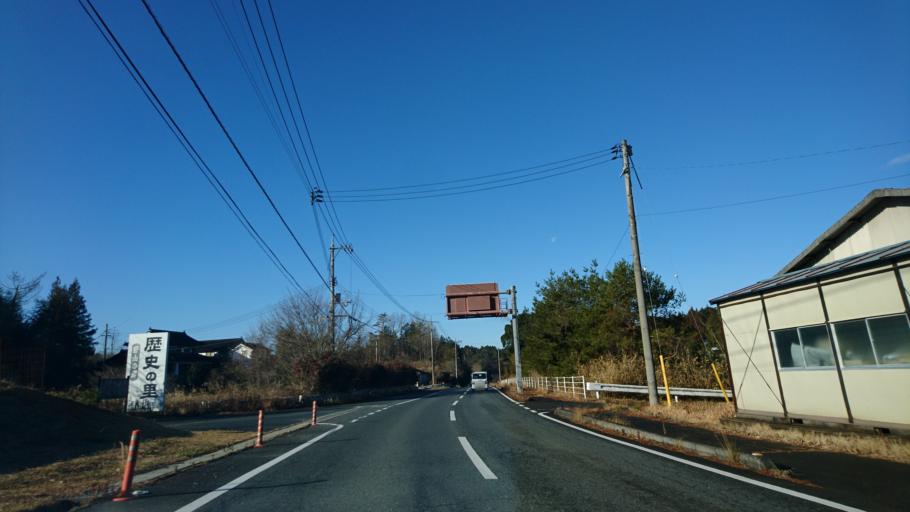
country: JP
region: Okayama
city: Takahashi
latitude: 34.8053
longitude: 133.6817
